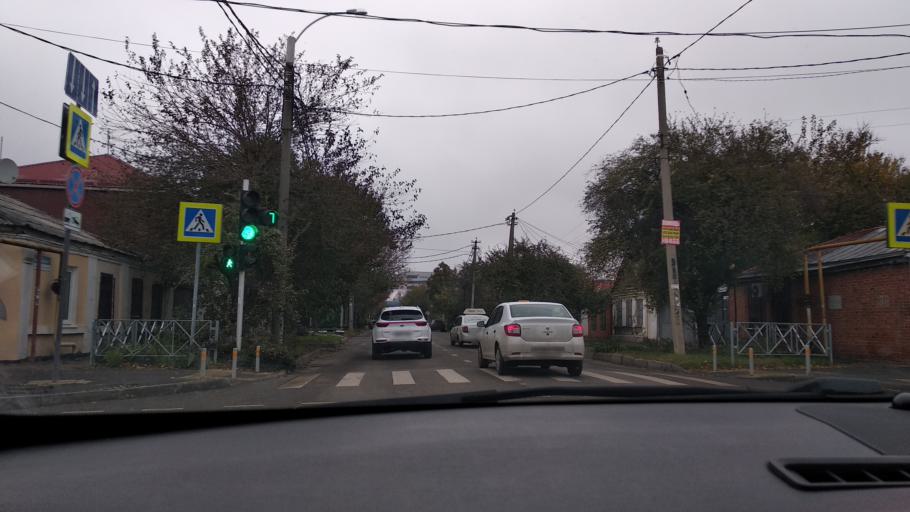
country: RU
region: Krasnodarskiy
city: Krasnodar
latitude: 45.0353
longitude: 38.9854
